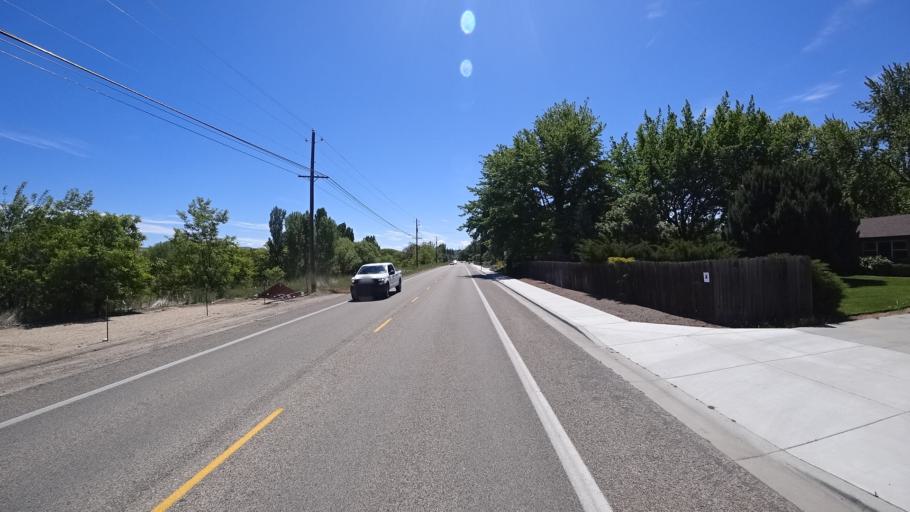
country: US
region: Idaho
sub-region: Ada County
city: Boise
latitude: 43.5696
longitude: -116.1509
